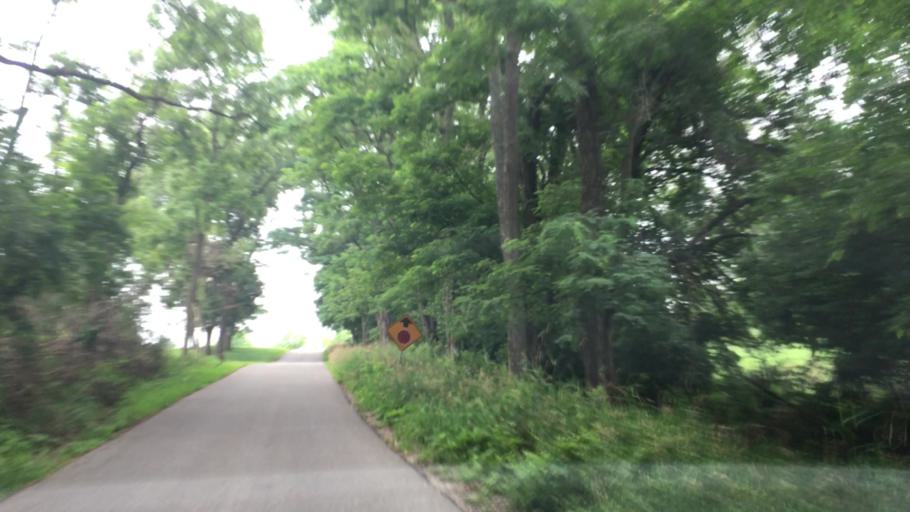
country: US
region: Iowa
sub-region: Johnson County
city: North Liberty
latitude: 41.7298
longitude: -91.5599
